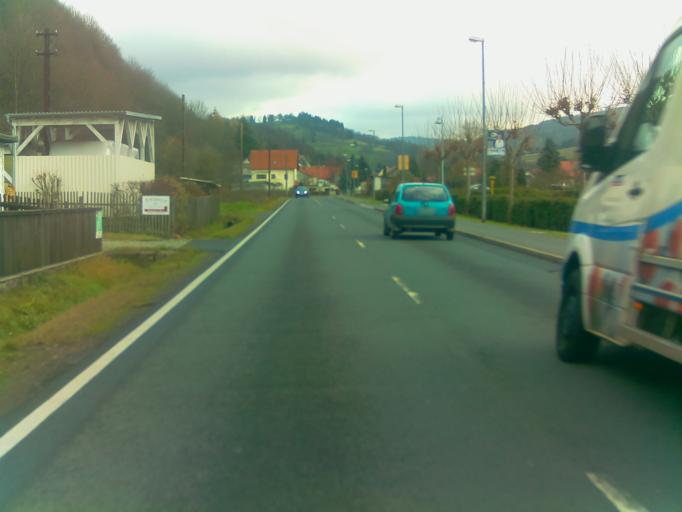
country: DE
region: Thuringia
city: Frauenwald
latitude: 50.5145
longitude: 10.8598
